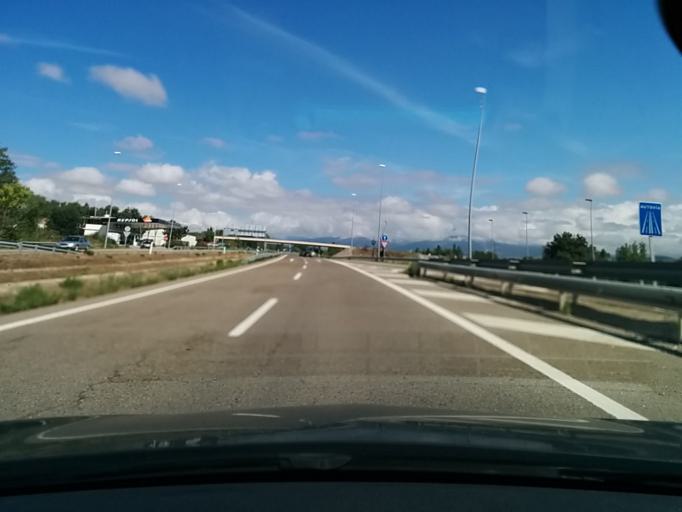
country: ES
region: Aragon
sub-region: Provincia de Huesca
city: Huesca
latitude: 42.1615
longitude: -0.4234
